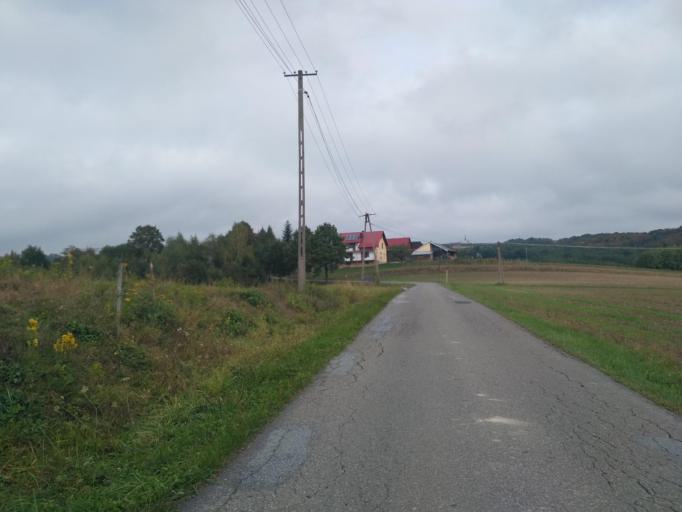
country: PL
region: Subcarpathian Voivodeship
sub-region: Powiat debicki
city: Brzostek
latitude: 49.9512
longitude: 21.4411
